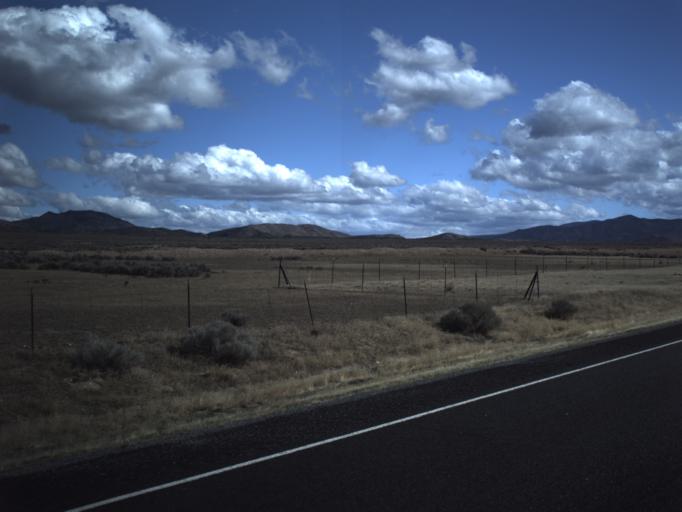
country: US
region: Utah
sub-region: Beaver County
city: Milford
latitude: 38.2654
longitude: -112.9548
